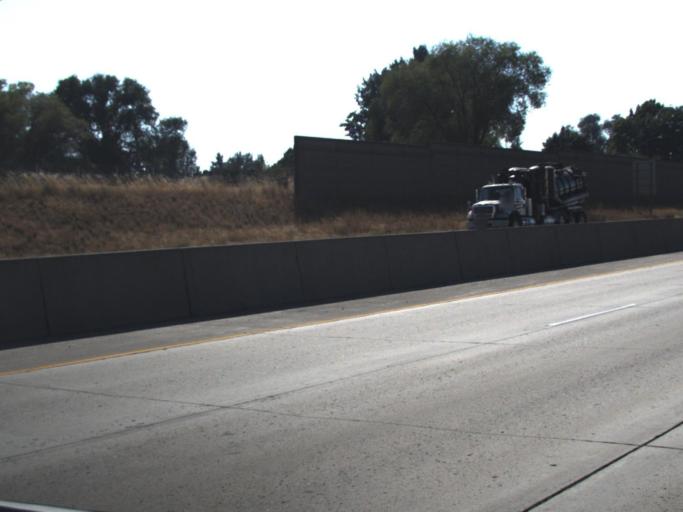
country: US
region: Washington
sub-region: Spokane County
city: Millwood
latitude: 47.6752
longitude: -117.2699
